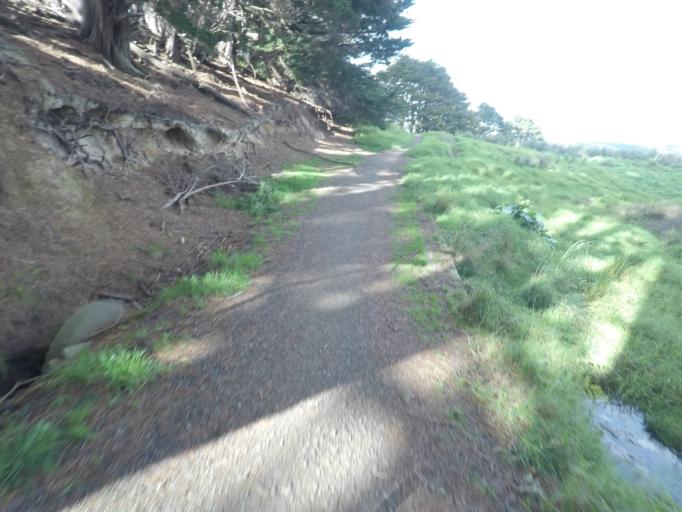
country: NZ
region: Auckland
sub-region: Auckland
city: Manukau City
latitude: -36.9963
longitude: 174.9140
